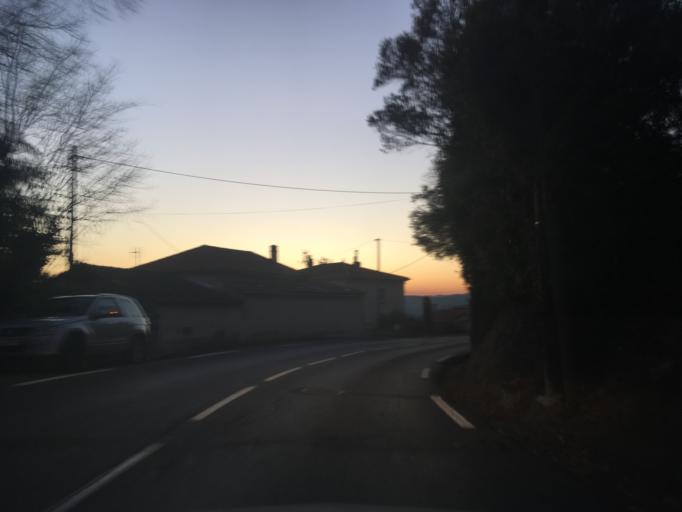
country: FR
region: Provence-Alpes-Cote d'Azur
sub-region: Departement du Var
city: Draguignan
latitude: 43.5383
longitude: 6.4747
